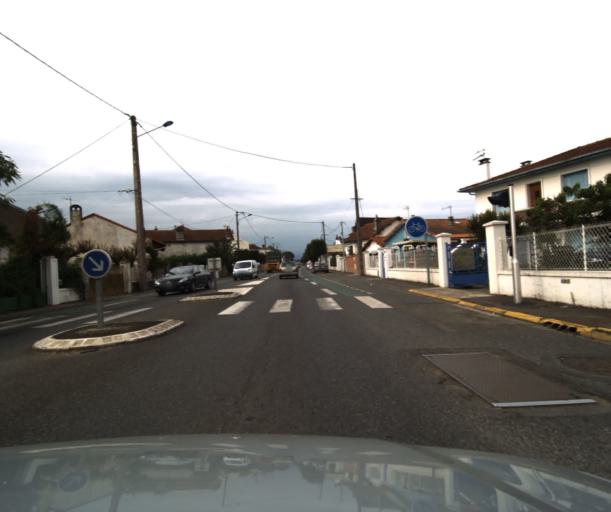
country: FR
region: Midi-Pyrenees
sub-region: Departement des Hautes-Pyrenees
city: Aureilhan
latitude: 43.2414
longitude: 0.0950
